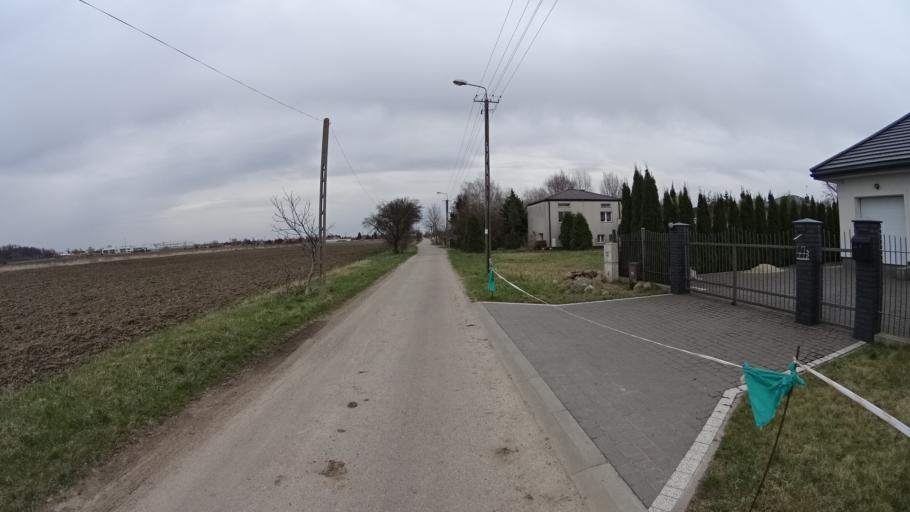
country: PL
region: Masovian Voivodeship
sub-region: Powiat warszawski zachodni
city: Stare Babice
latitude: 52.2441
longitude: 20.8086
